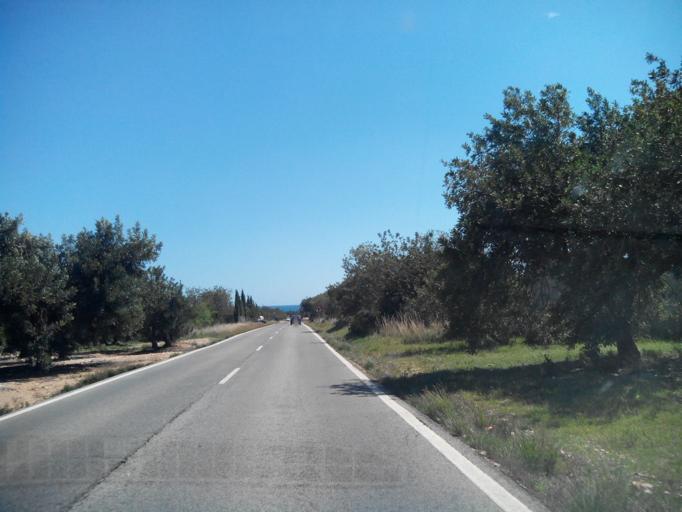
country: ES
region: Catalonia
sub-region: Provincia de Tarragona
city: Riudecanyes
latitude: 41.0696
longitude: 0.9805
